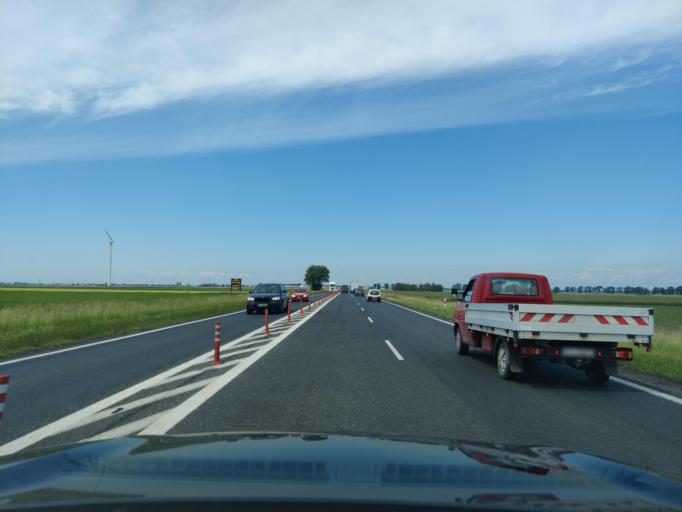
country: PL
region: Greater Poland Voivodeship
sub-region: Powiat grodziski
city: Granowo
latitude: 52.2213
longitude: 16.5748
